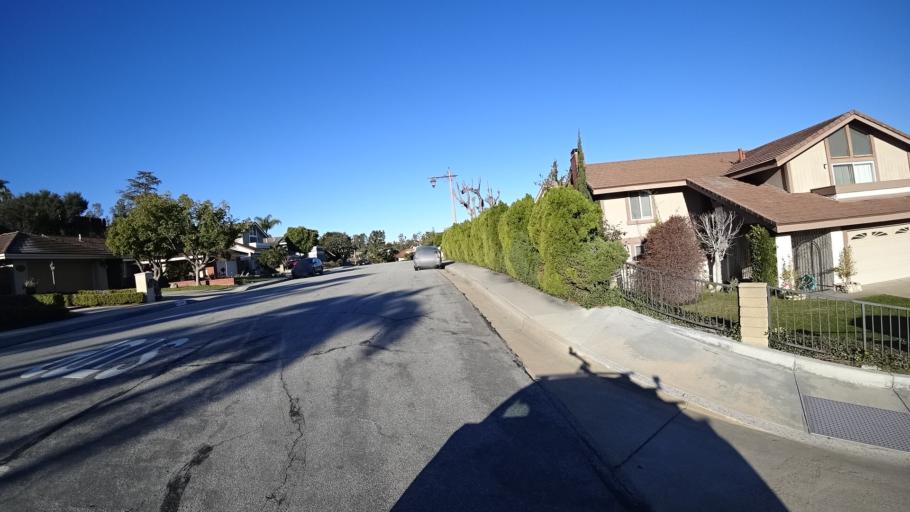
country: US
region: California
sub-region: Orange County
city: Villa Park
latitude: 33.8413
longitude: -117.7936
